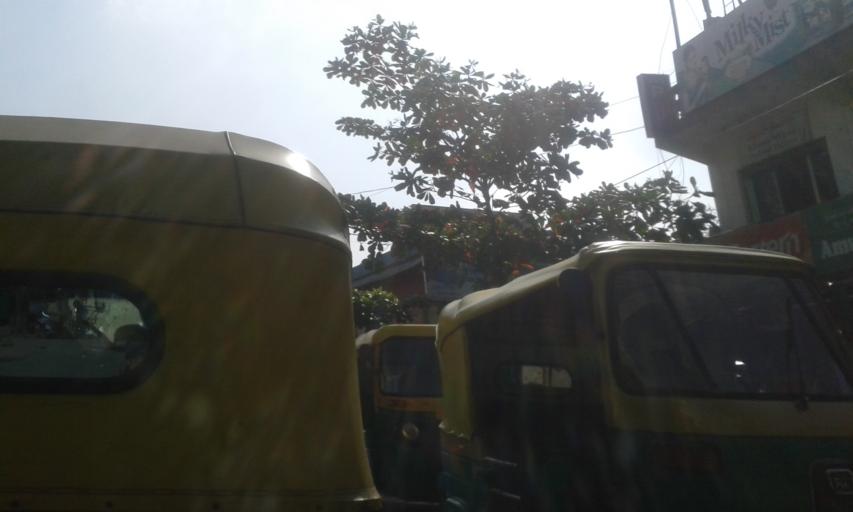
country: IN
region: Karnataka
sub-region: Bangalore Urban
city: Bangalore
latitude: 12.9508
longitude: 77.6234
